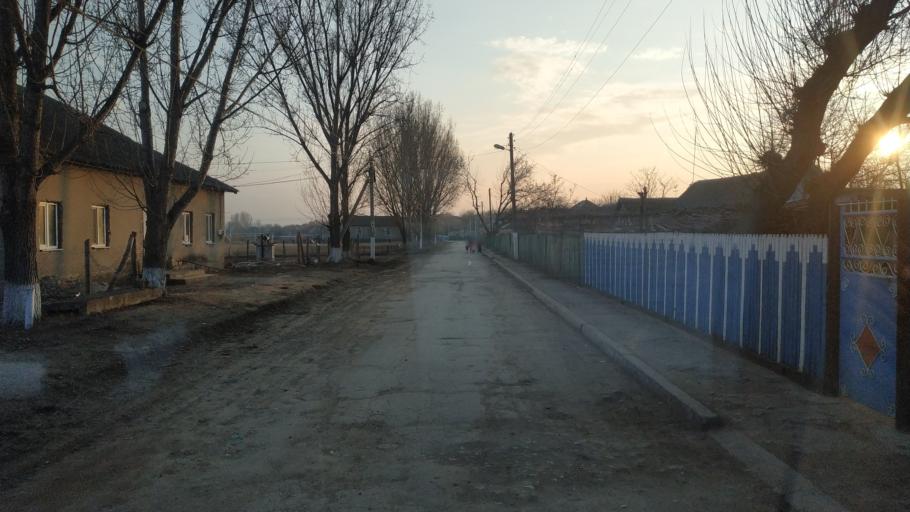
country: MD
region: Hincesti
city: Dancu
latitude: 46.7126
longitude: 28.3472
